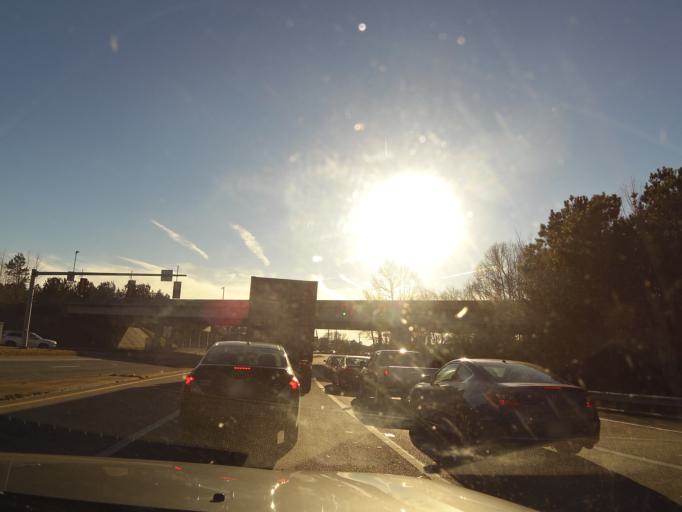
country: US
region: Virginia
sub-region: City of Suffolk
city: South Suffolk
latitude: 36.7272
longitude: -76.6318
